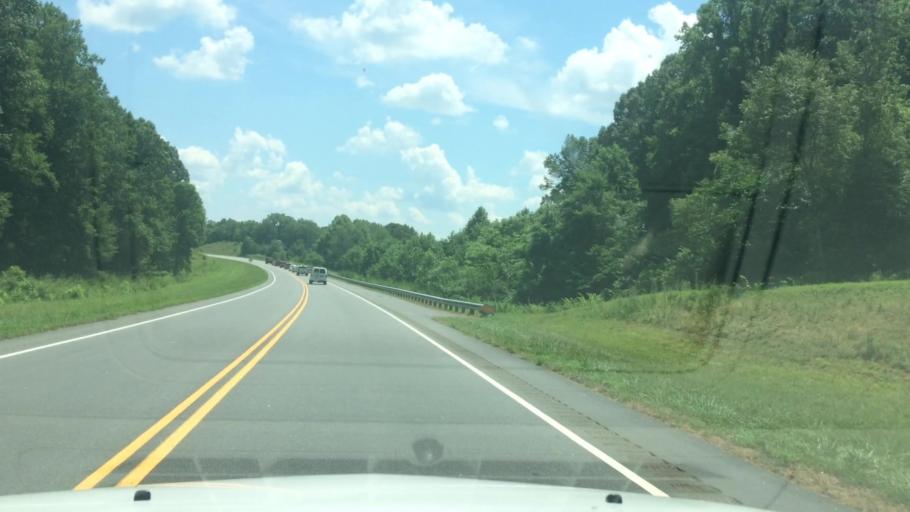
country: US
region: North Carolina
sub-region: Alexander County
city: Stony Point
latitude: 35.8637
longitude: -81.0594
